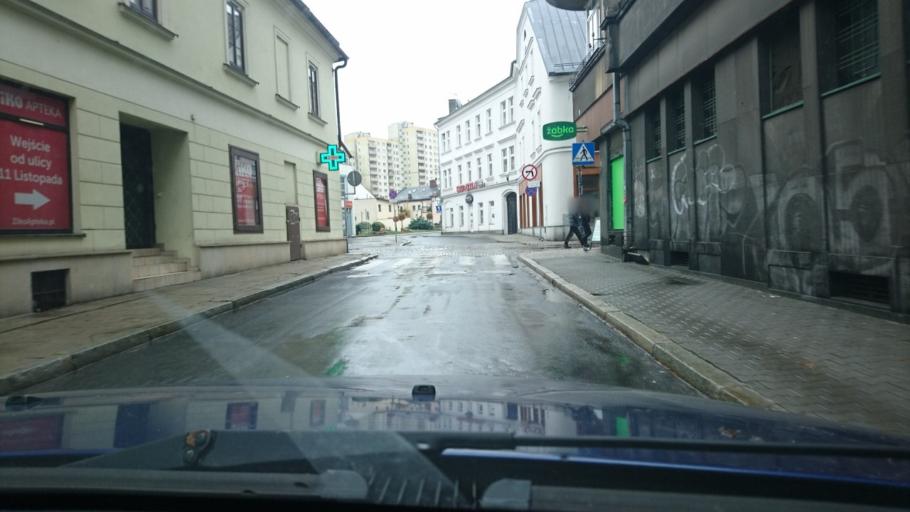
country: PL
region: Silesian Voivodeship
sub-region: Bielsko-Biala
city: Bielsko-Biala
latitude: 49.8234
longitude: 19.0525
